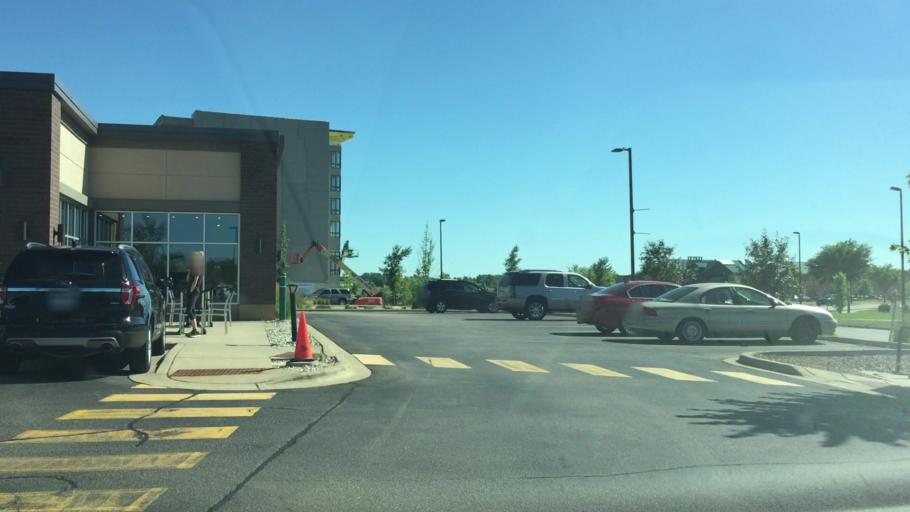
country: US
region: Wisconsin
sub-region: Dane County
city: Sun Prairie
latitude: 43.1668
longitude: -89.2700
